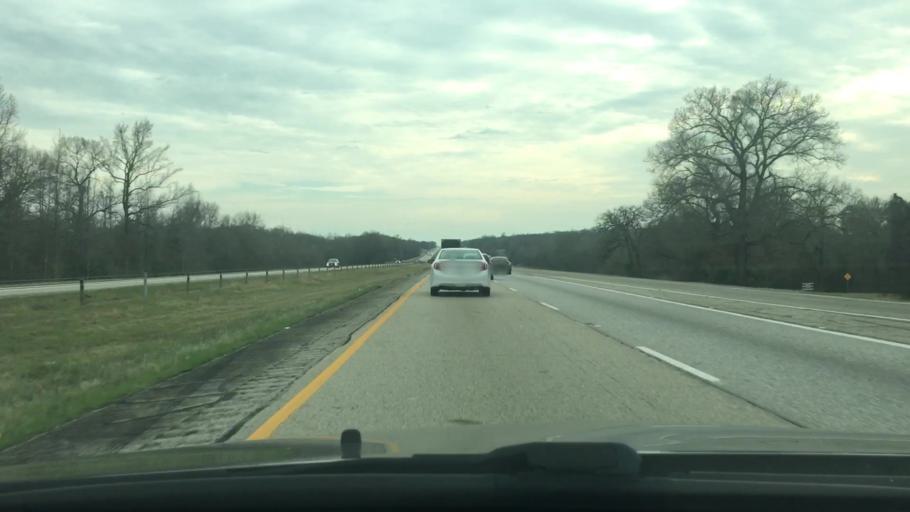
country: US
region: Texas
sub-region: Leon County
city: Centerville
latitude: 31.1927
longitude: -95.9930
